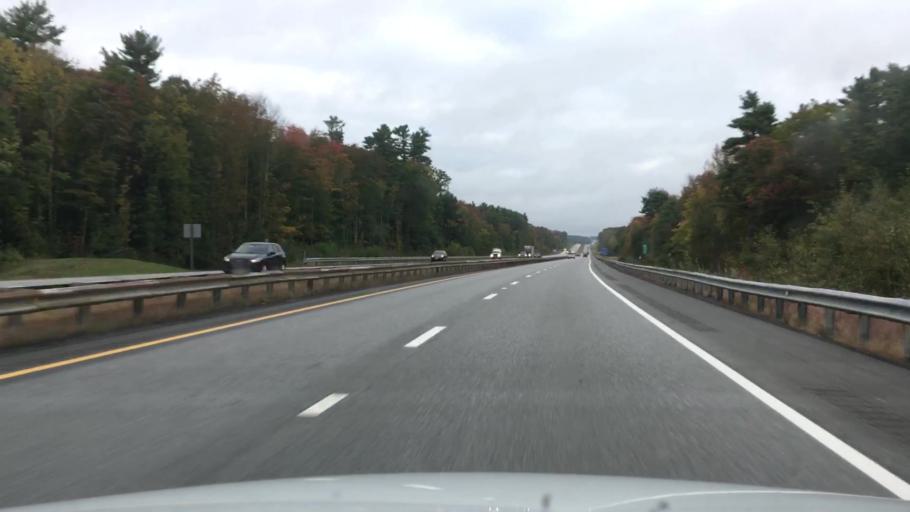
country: US
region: Maine
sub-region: Cumberland County
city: Cumberland Center
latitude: 43.7675
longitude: -70.3122
